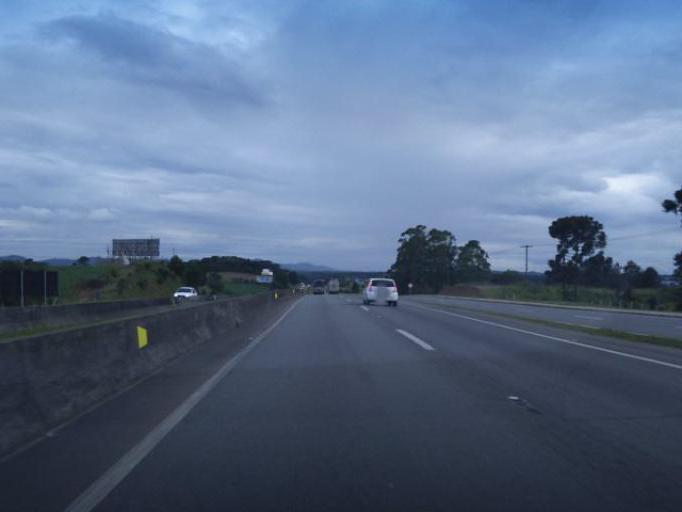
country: BR
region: Parana
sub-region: Sao Jose Dos Pinhais
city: Sao Jose dos Pinhais
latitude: -25.6228
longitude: -49.1669
